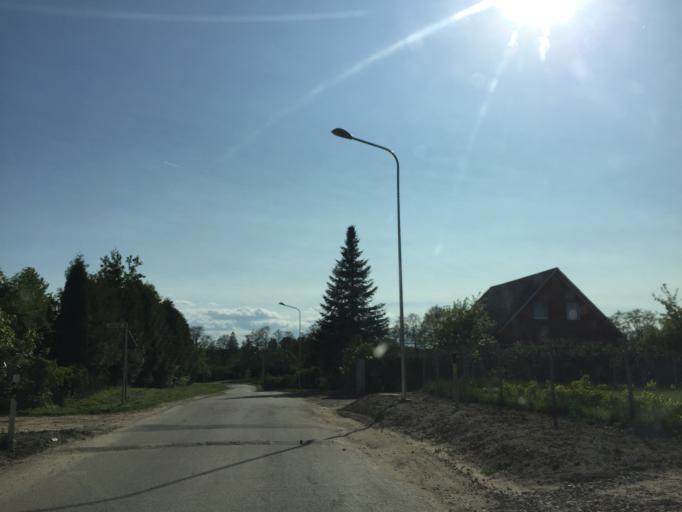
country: LV
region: Salaspils
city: Salaspils
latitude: 56.8228
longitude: 24.4261
